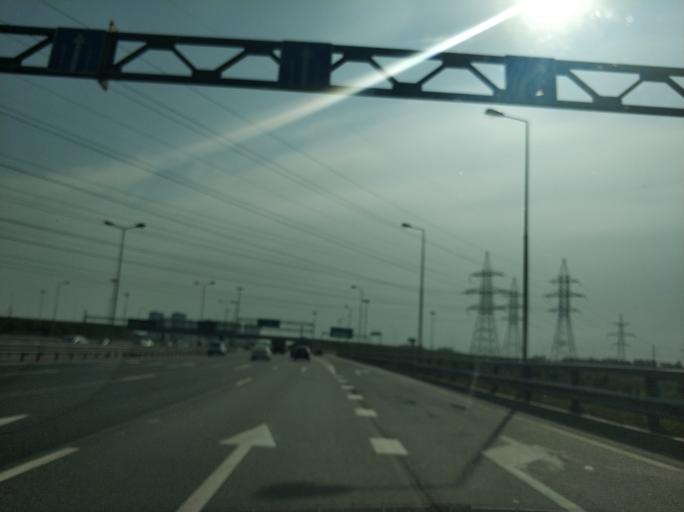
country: RU
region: Leningrad
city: Murino
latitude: 60.0195
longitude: 30.4563
